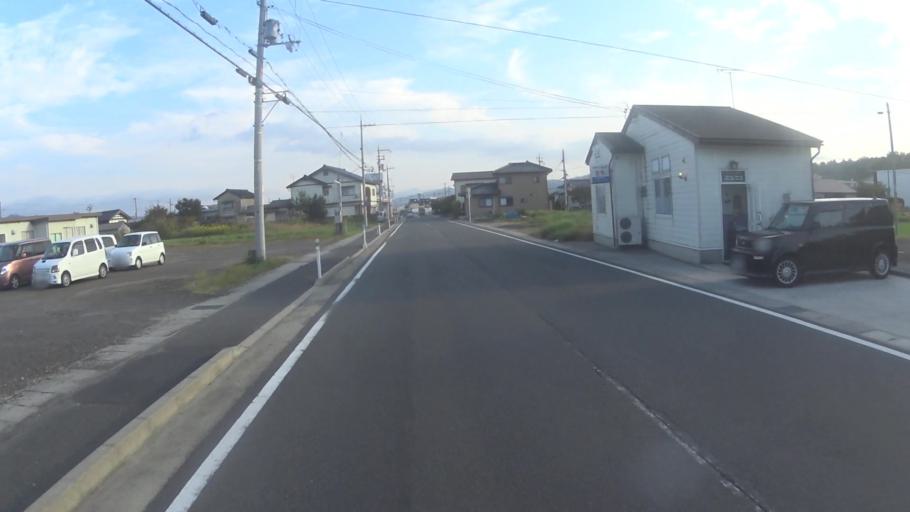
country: JP
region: Kyoto
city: Miyazu
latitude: 35.6220
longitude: 135.0741
